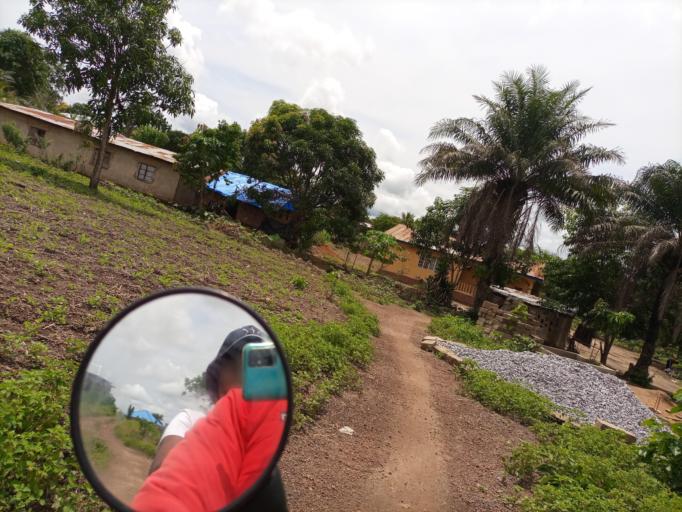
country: SL
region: Southern Province
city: Baoma
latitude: 7.9813
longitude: -11.7201
